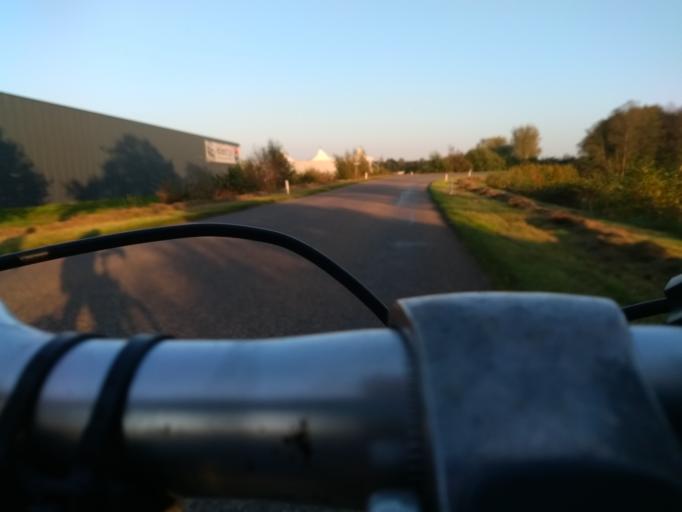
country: NL
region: Drenthe
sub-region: Gemeente Assen
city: Assen
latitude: 52.9706
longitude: 6.5571
